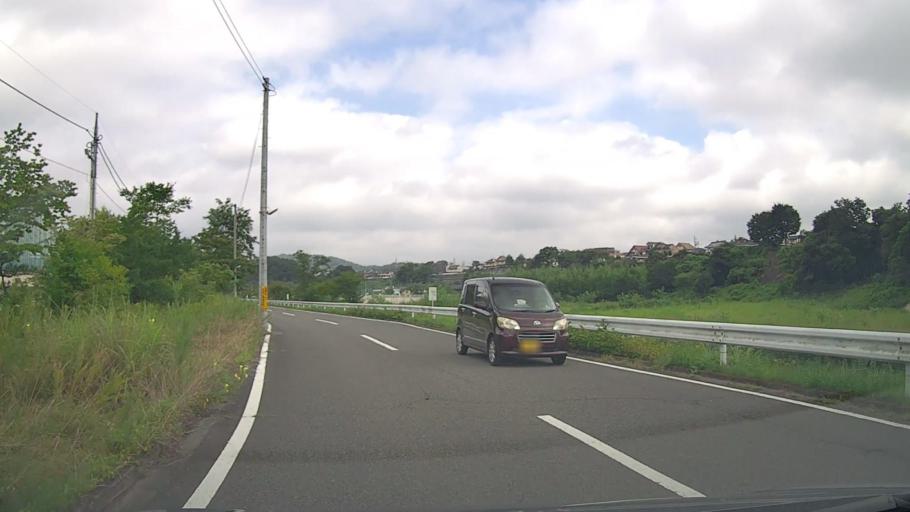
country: JP
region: Tokyo
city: Itsukaichi
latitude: 35.7208
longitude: 139.2631
